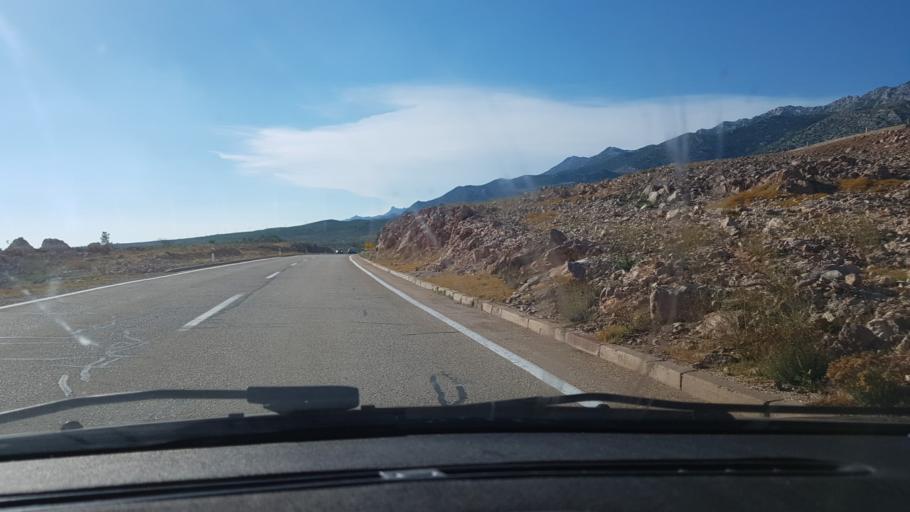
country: HR
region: Zadarska
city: Obrovac
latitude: 44.2206
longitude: 15.6523
